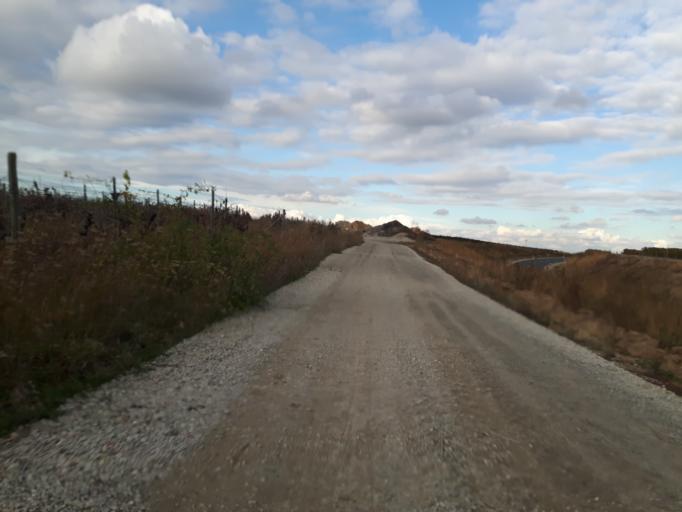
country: DE
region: Rheinland-Pfalz
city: Kirchheim an der Weinstrasse
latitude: 49.5441
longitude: 8.1719
